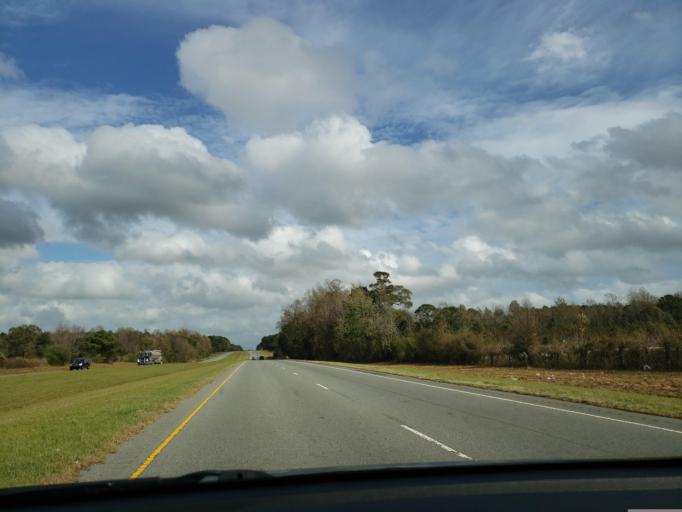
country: US
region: North Carolina
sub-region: Duplin County
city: Kenansville
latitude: 34.9293
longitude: -78.0041
